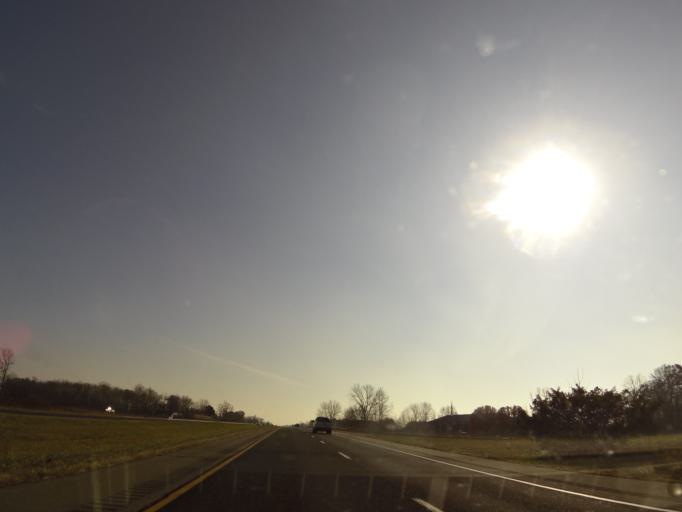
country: US
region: Indiana
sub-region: Hancock County
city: New Palestine
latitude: 39.6450
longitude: -85.9127
